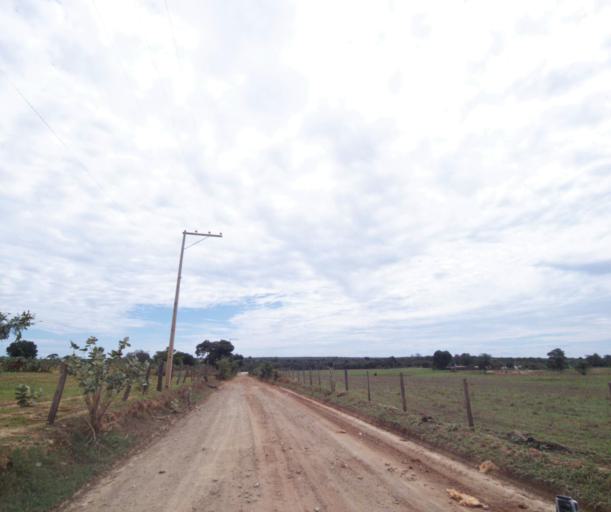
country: BR
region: Bahia
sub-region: Carinhanha
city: Carinhanha
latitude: -14.2189
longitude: -44.2901
